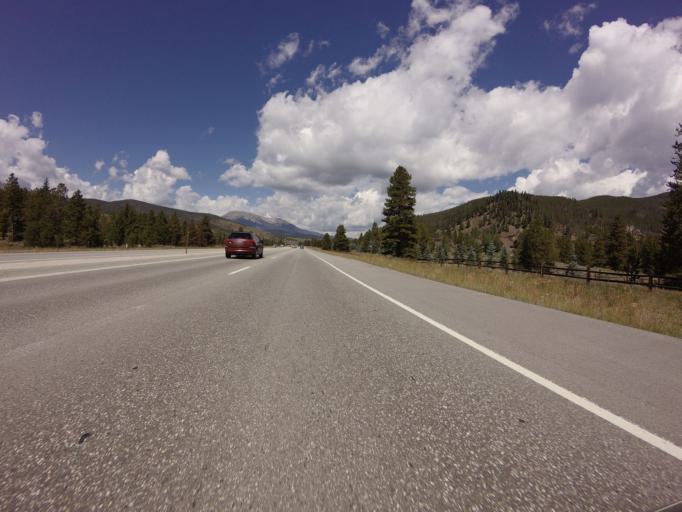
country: US
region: Colorado
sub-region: Summit County
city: Frisco
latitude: 39.5508
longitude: -106.0423
